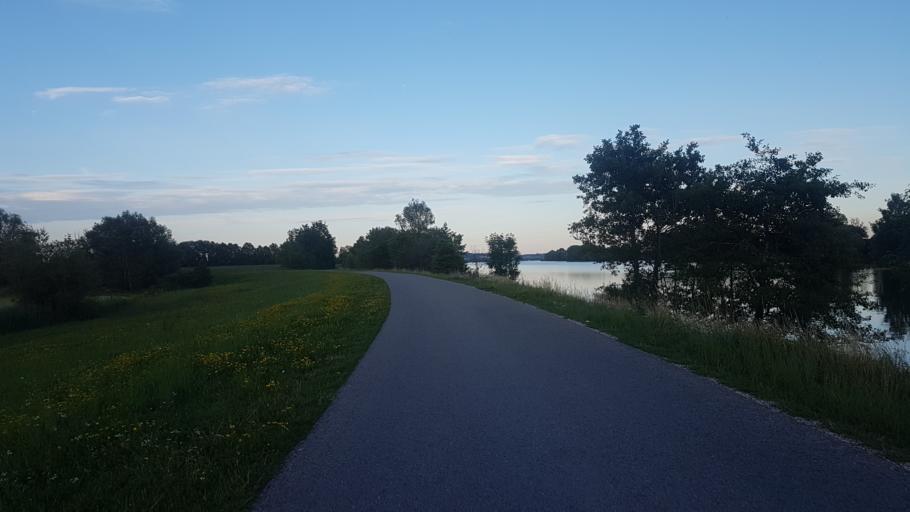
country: DE
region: Bavaria
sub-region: Regierungsbezirk Mittelfranken
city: Muhr am See
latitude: 49.1422
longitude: 10.6929
